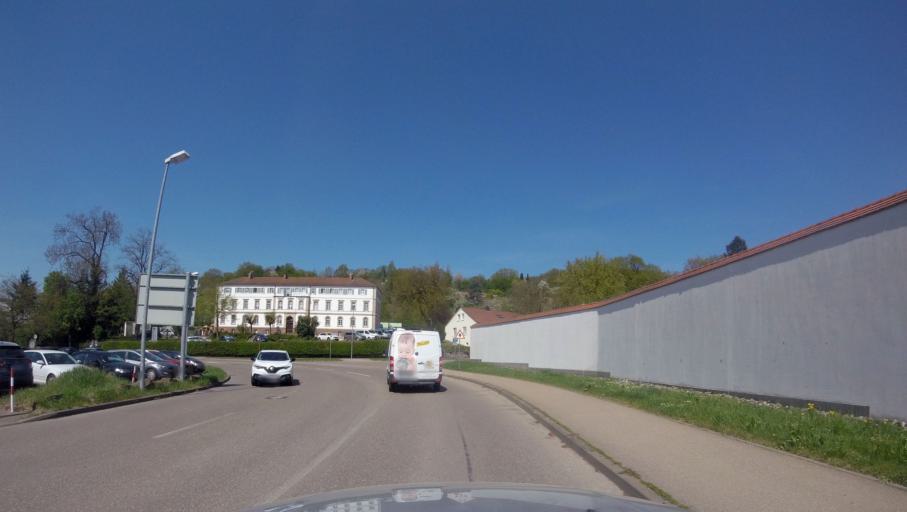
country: DE
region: Baden-Wuerttemberg
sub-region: Regierungsbezirk Stuttgart
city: Schwabisch Gmund
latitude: 48.8046
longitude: 9.8098
